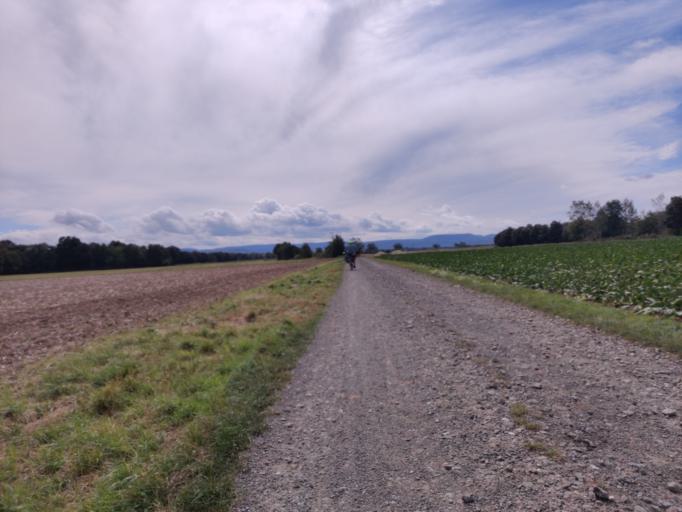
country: DE
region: Lower Saxony
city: Langelsheim
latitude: 51.9903
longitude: 10.3701
